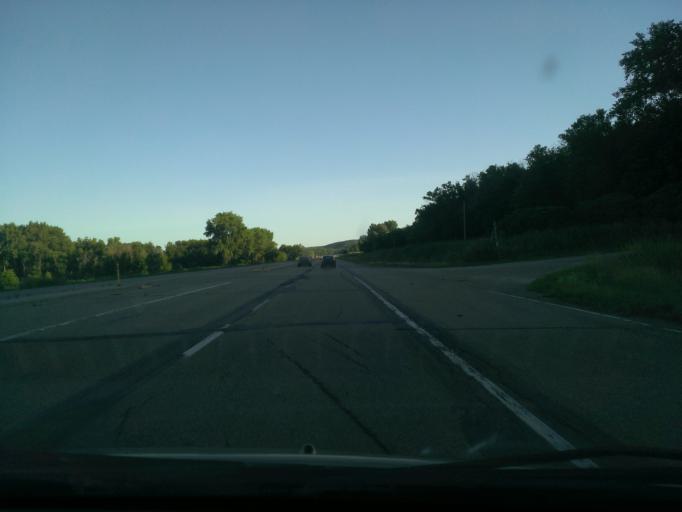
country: US
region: Minnesota
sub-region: Nicollet County
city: North Mankato
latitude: 44.2416
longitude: -94.0274
